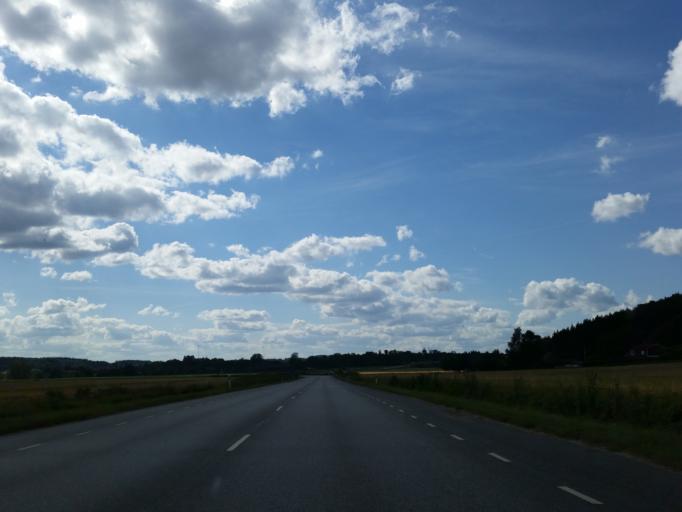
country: SE
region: Soedermanland
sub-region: Trosa Kommun
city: Vagnharad
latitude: 58.9464
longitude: 17.5257
